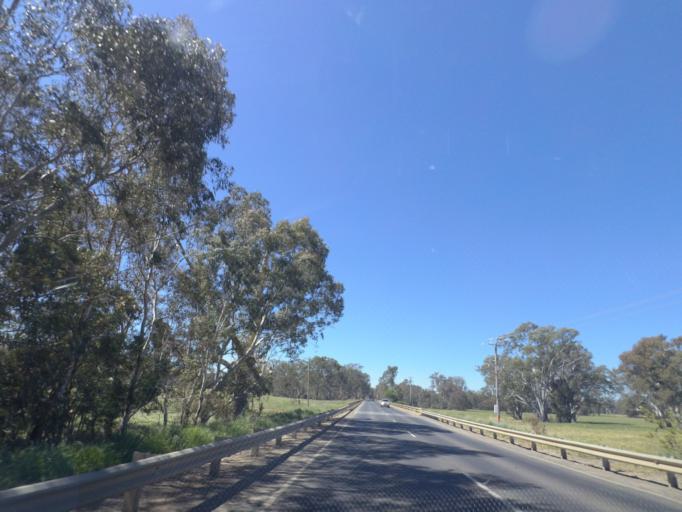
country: AU
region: Victoria
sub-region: Murrindindi
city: Kinglake West
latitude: -37.0271
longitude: 145.1088
